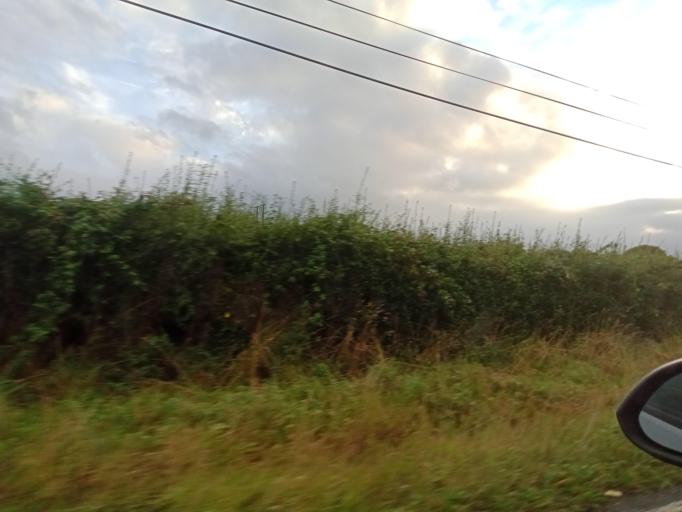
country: IE
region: Leinster
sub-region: Uibh Fhaili
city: Tullamore
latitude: 53.1456
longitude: -7.4811
